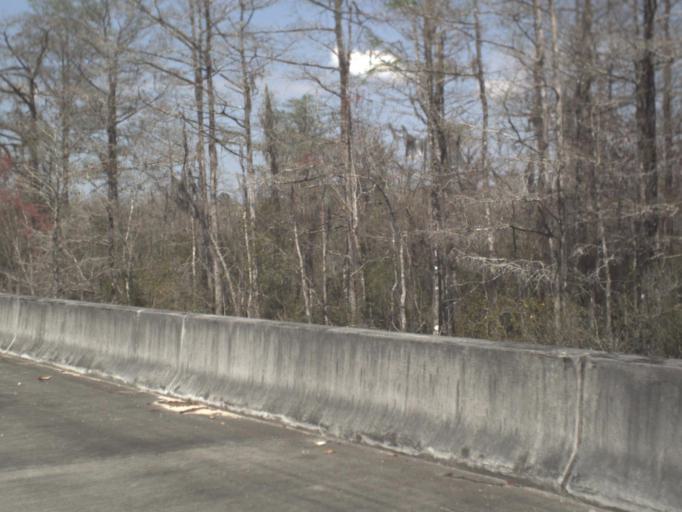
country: US
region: Florida
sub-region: Gadsden County
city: Quincy
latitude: 30.3878
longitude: -84.6655
